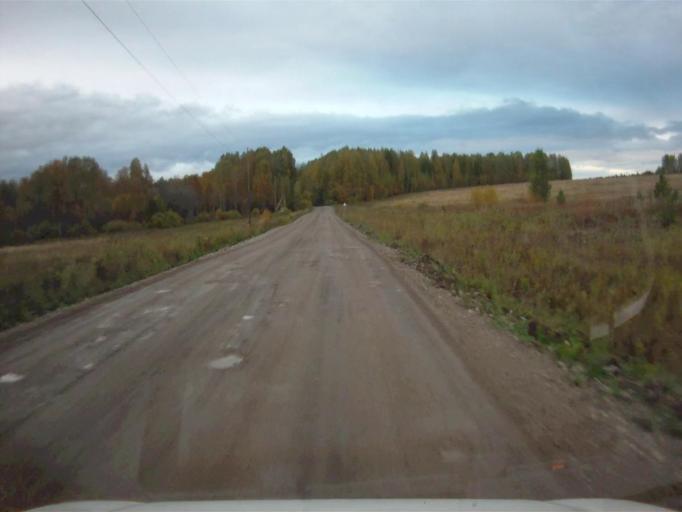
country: RU
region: Sverdlovsk
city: Mikhaylovsk
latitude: 56.1909
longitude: 59.1894
